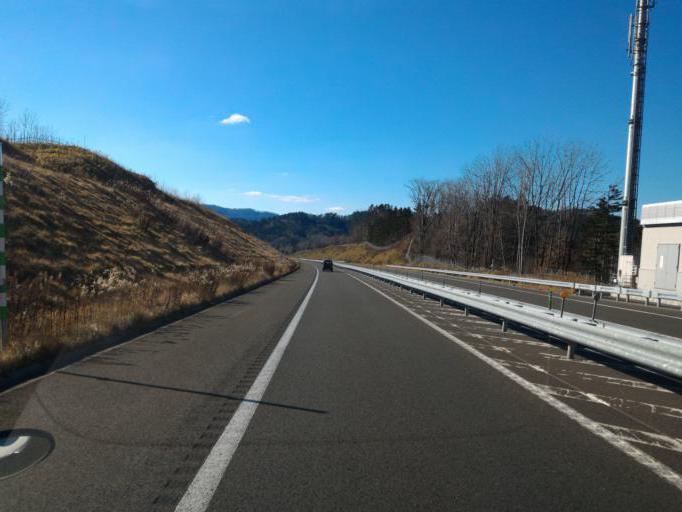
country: JP
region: Hokkaido
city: Shimo-furano
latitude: 42.9420
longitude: 142.2166
